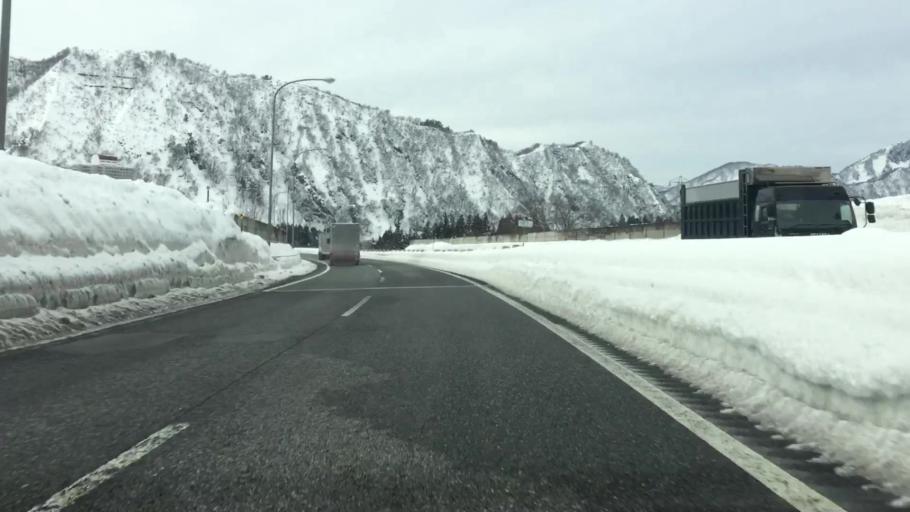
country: JP
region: Niigata
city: Shiozawa
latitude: 36.9059
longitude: 138.8460
